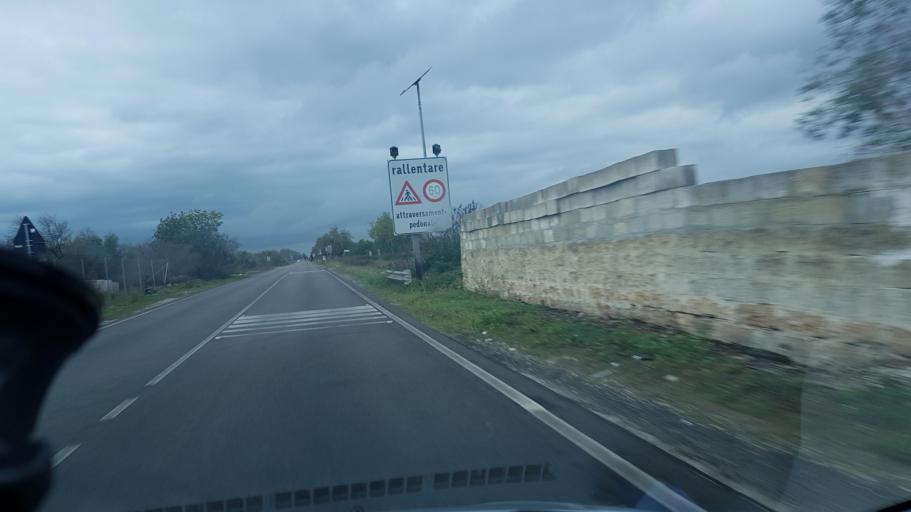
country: IT
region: Apulia
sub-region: Provincia di Lecce
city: Arnesano
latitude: 40.3611
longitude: 18.0989
